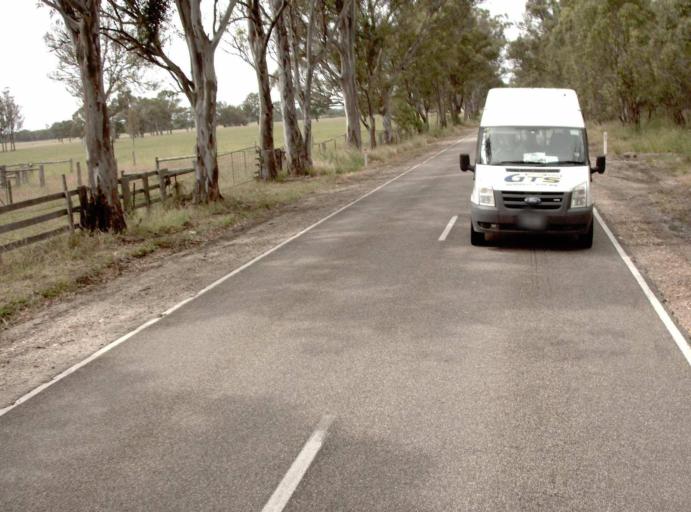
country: AU
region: Victoria
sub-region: Wellington
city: Sale
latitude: -37.9084
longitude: 147.0790
